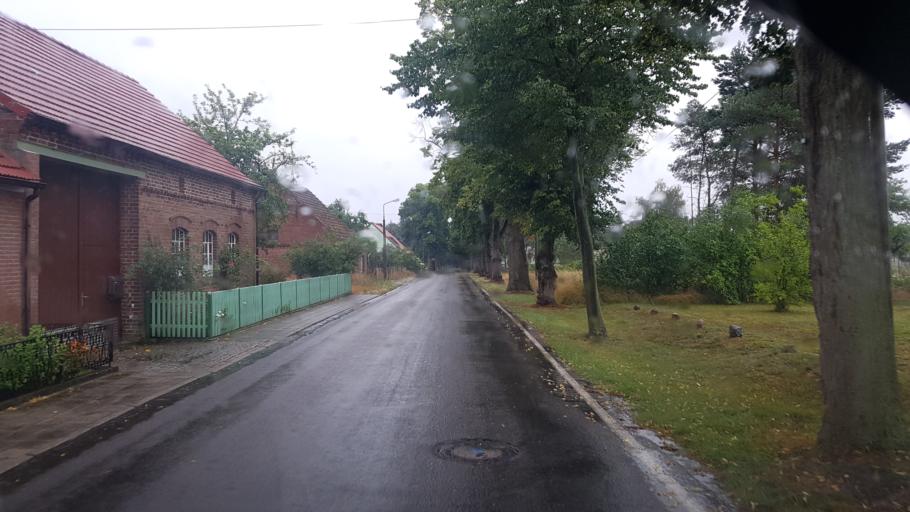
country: DE
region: Brandenburg
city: Dahme
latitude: 51.9435
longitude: 13.3955
